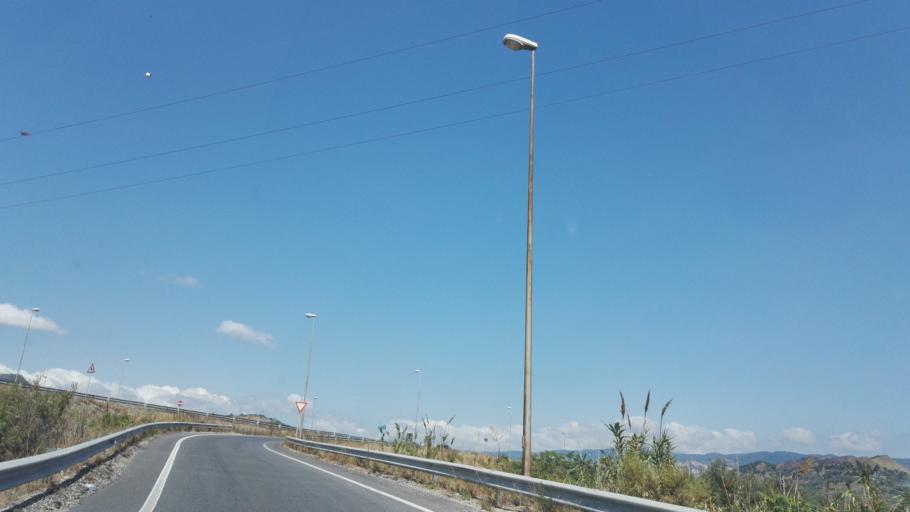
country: IT
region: Calabria
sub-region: Provincia di Reggio Calabria
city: Gioiosa Ionica
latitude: 38.3113
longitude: 16.3044
